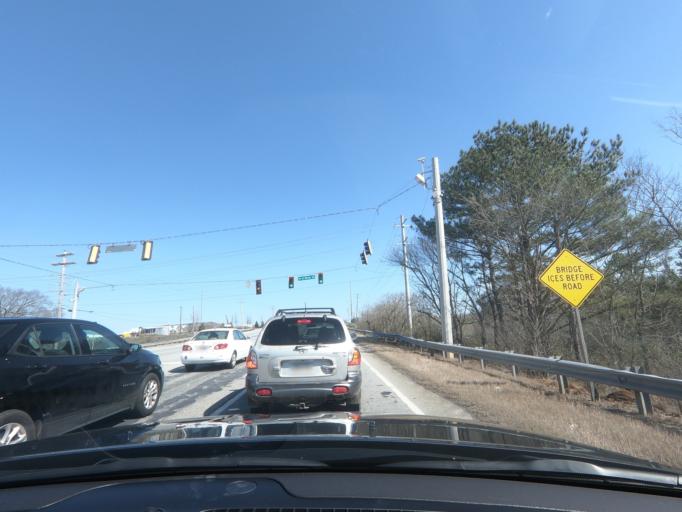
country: US
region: Georgia
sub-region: Gordon County
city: Calhoun
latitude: 34.4807
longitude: -84.9529
